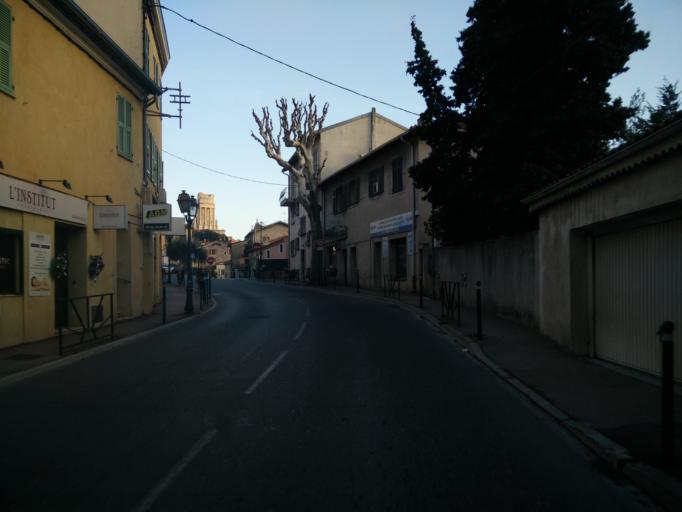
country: FR
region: Provence-Alpes-Cote d'Azur
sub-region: Departement des Alpes-Maritimes
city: La Turbie
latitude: 43.7456
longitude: 7.3983
